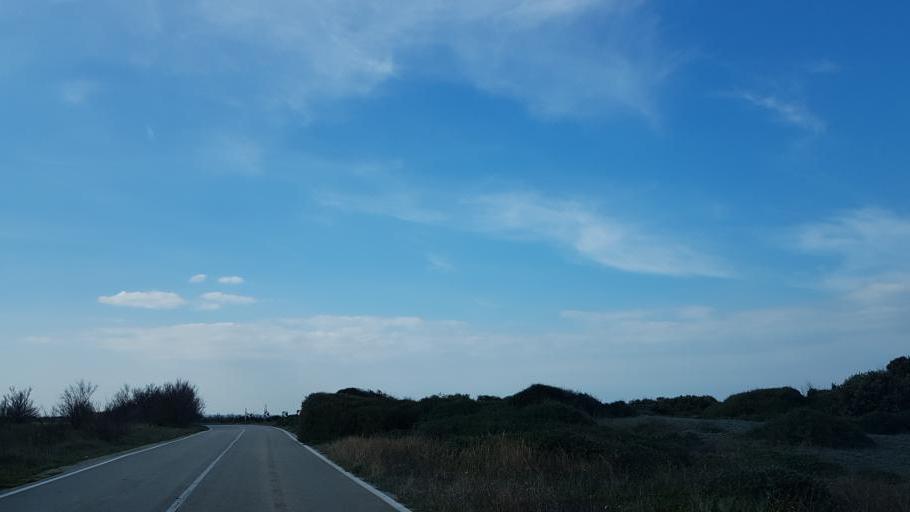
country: IT
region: Apulia
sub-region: Provincia di Brindisi
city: Brindisi
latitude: 40.6880
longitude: 17.8549
